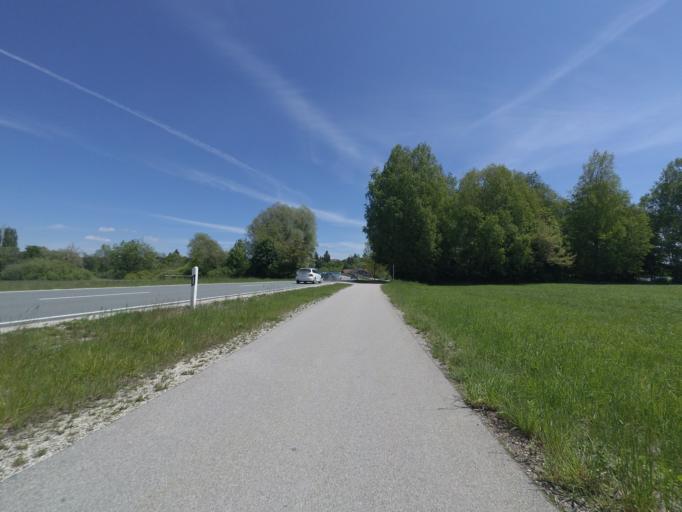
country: DE
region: Bavaria
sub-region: Upper Bavaria
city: Taching am See
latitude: 47.9538
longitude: 12.7476
